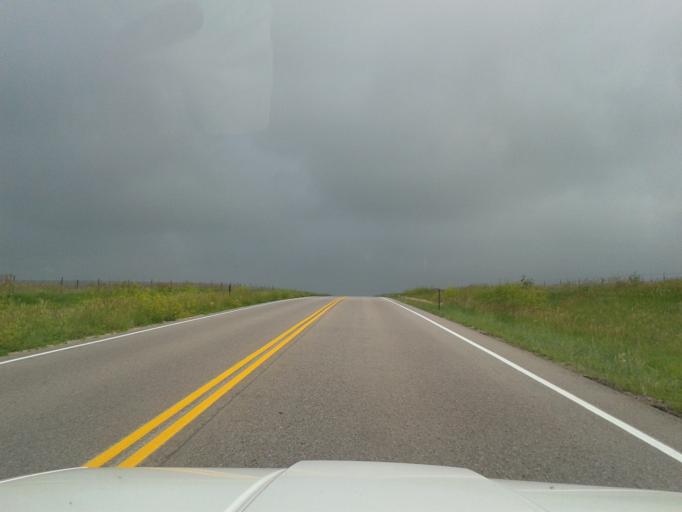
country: US
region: Colorado
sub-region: Elbert County
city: Ponderosa Park
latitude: 39.3017
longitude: -104.7357
